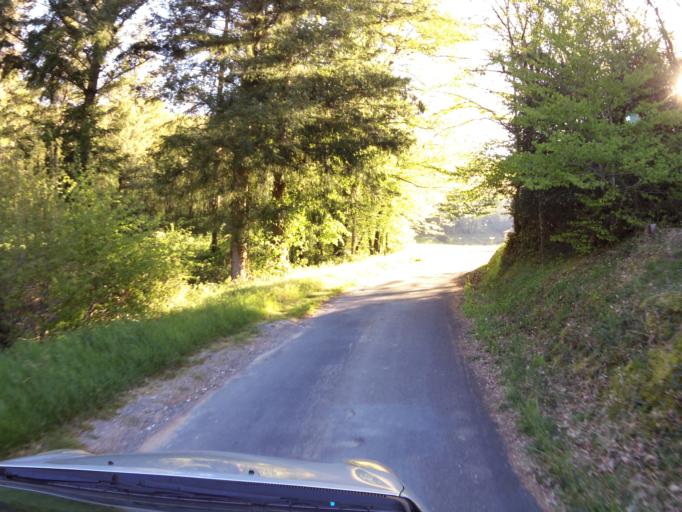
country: FR
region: Aquitaine
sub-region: Departement de la Dordogne
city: Carsac-Aillac
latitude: 44.8196
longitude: 1.2990
